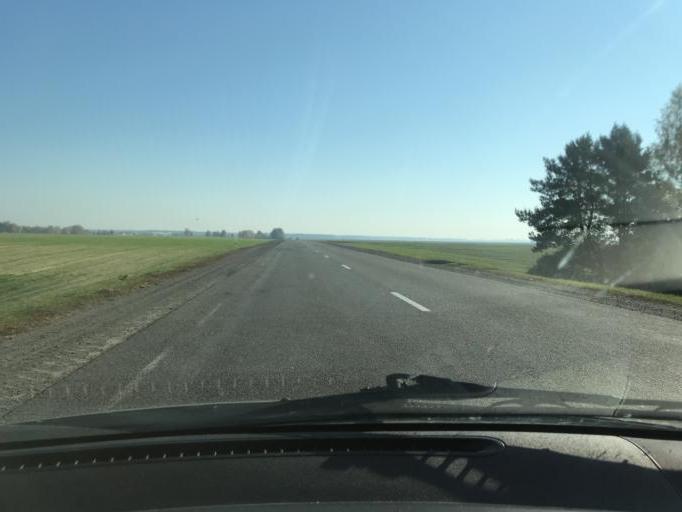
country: BY
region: Brest
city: Luninyets
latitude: 52.2573
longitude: 27.0421
